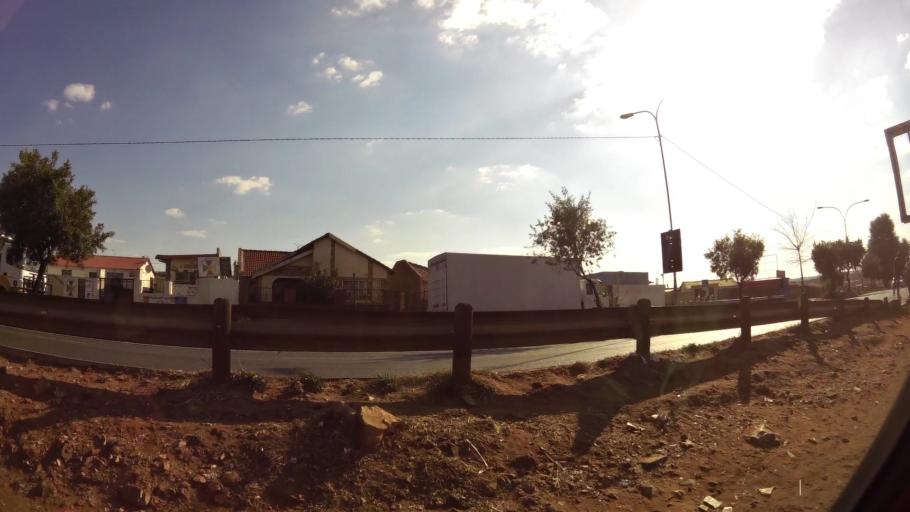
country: ZA
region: Gauteng
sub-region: City of Johannesburg Metropolitan Municipality
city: Soweto
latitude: -26.2253
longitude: 27.8731
